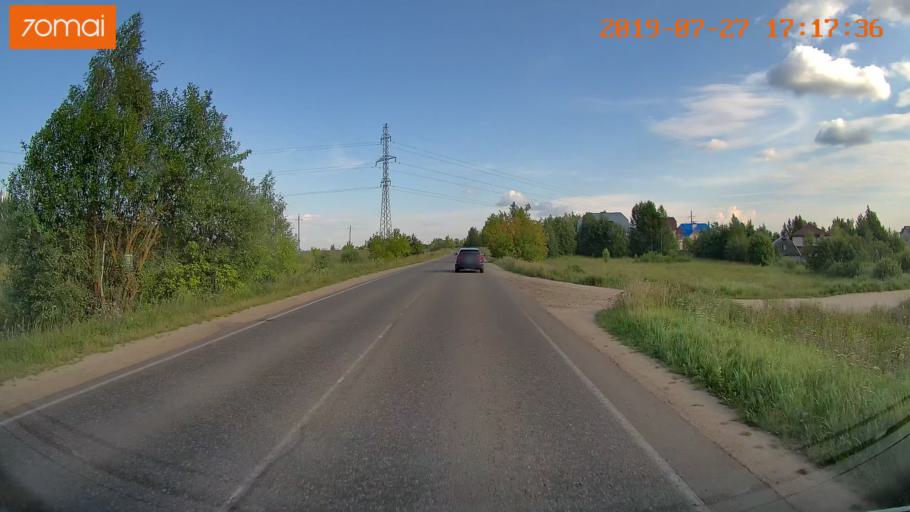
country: RU
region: Ivanovo
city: Novo-Talitsy
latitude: 57.0358
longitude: 40.8964
